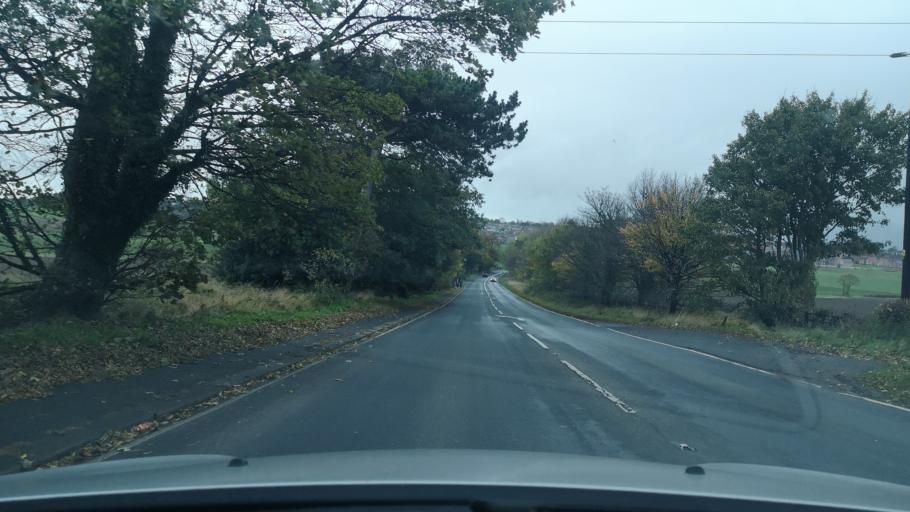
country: GB
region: England
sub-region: City and Borough of Wakefield
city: Low Ackworth
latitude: 53.6691
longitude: -1.3241
